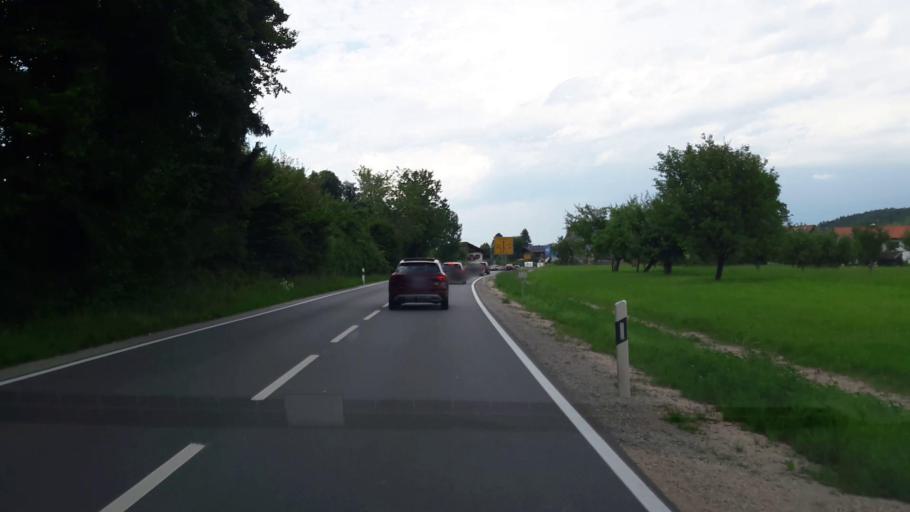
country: DE
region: Bavaria
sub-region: Upper Bavaria
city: Anger
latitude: 47.7980
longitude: 12.8664
